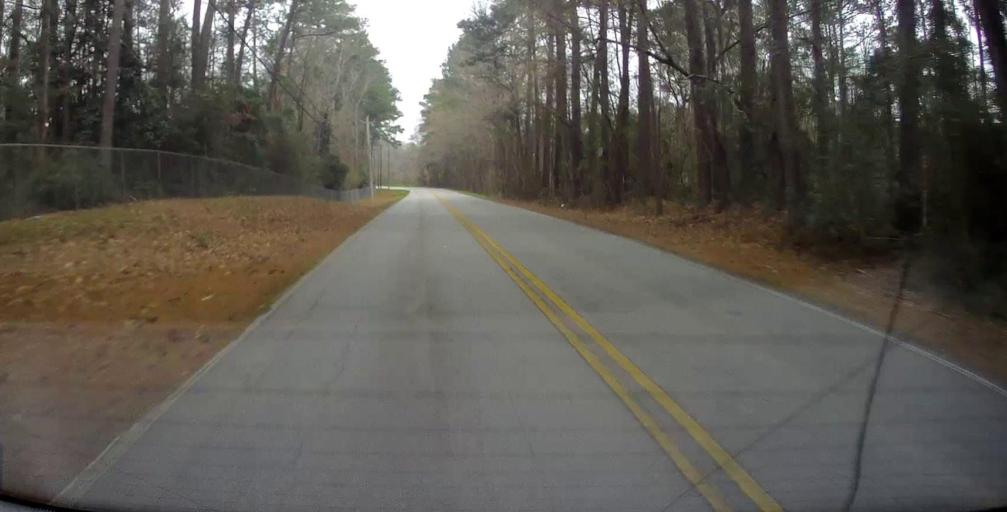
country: US
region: Georgia
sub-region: Bibb County
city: Macon
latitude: 32.8822
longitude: -83.7250
